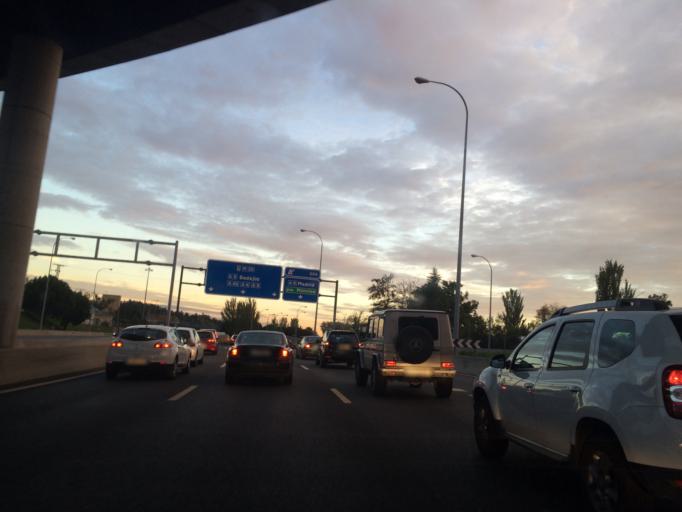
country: ES
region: Madrid
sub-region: Provincia de Madrid
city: Moncloa-Aravaca
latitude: 40.4525
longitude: -3.7434
